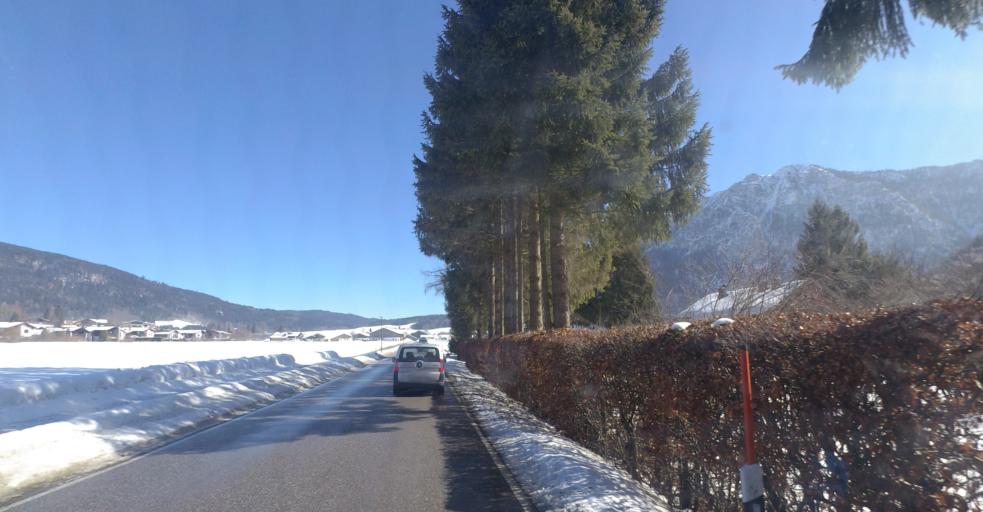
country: DE
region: Bavaria
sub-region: Upper Bavaria
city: Inzell
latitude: 47.7617
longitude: 12.7566
